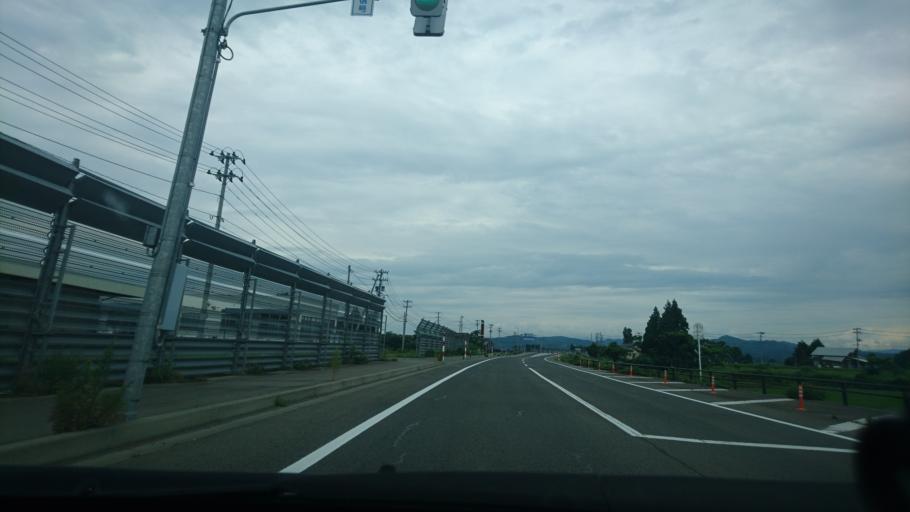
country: JP
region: Akita
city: Omagari
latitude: 39.5146
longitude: 140.3787
